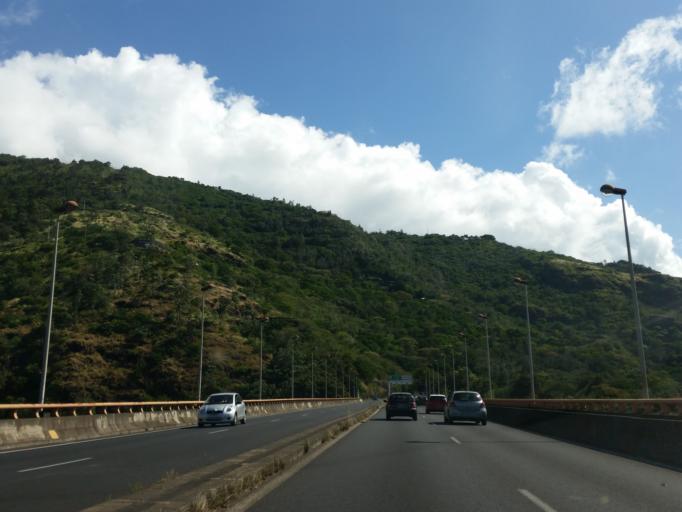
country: RE
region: Reunion
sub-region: Reunion
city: Saint-Denis
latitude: -20.8881
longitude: 55.4438
